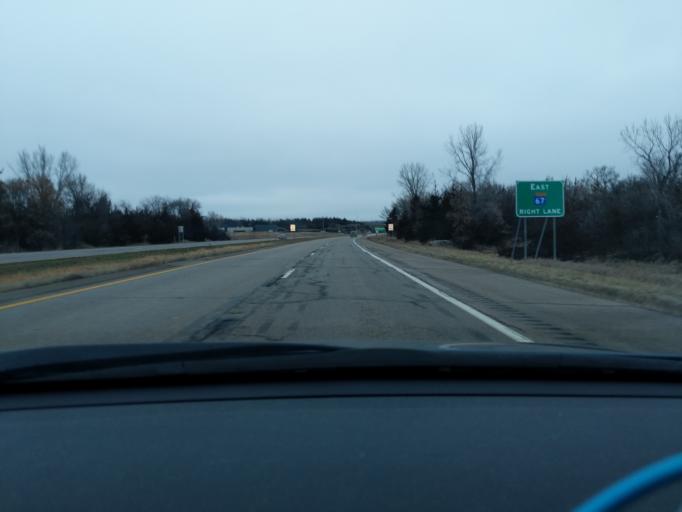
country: US
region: Minnesota
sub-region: Yellow Medicine County
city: Granite Falls
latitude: 44.7983
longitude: -95.5482
